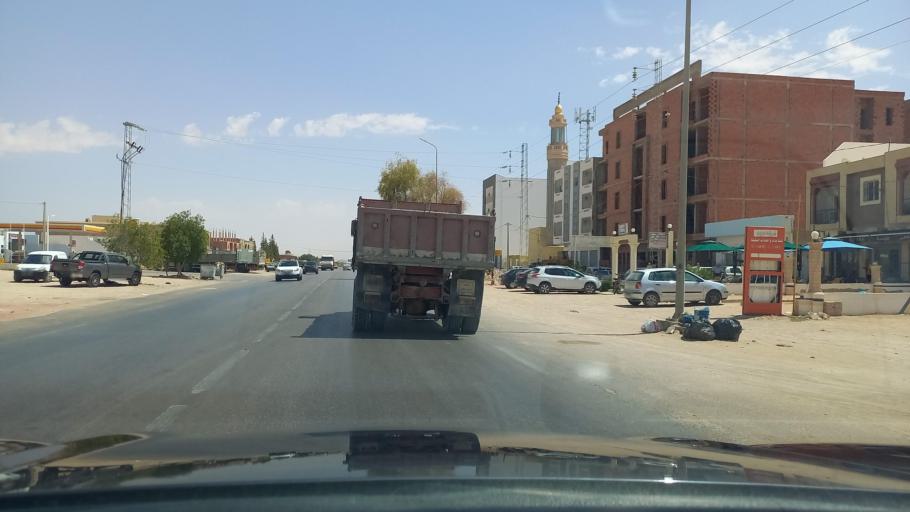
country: TN
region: Madanin
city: Medenine
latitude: 33.3655
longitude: 10.4586
